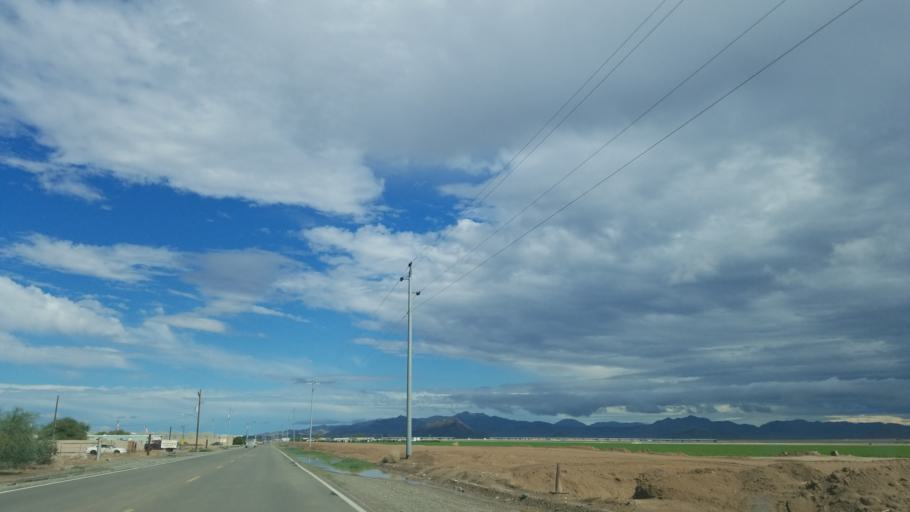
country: US
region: Arizona
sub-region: La Paz County
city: Salome
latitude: 33.6665
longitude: -113.7672
